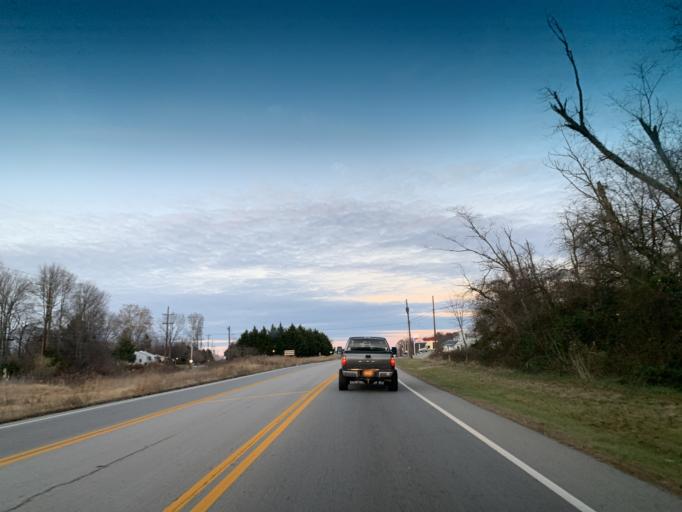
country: US
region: Maryland
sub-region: Cecil County
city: Elkton
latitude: 39.5109
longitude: -75.8282
